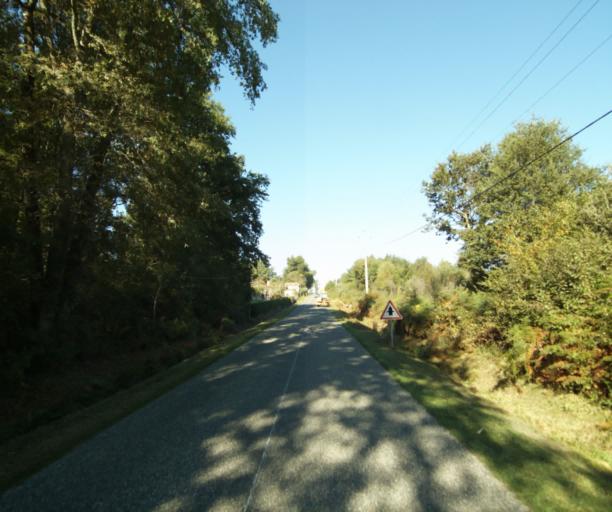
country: FR
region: Aquitaine
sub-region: Departement des Landes
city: Gabarret
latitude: 43.9551
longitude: -0.0166
